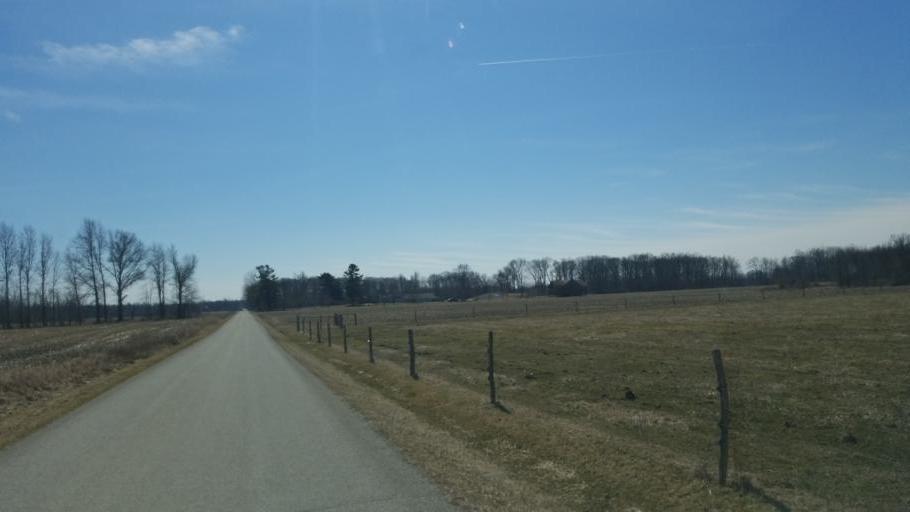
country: US
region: Ohio
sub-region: Crawford County
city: Galion
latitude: 40.7088
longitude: -82.7556
